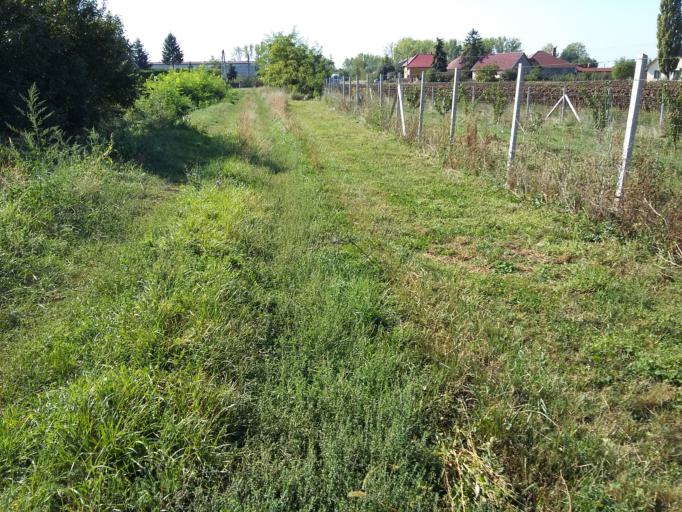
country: HU
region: Borsod-Abauj-Zemplen
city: Bekecs
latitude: 48.1491
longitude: 21.1608
